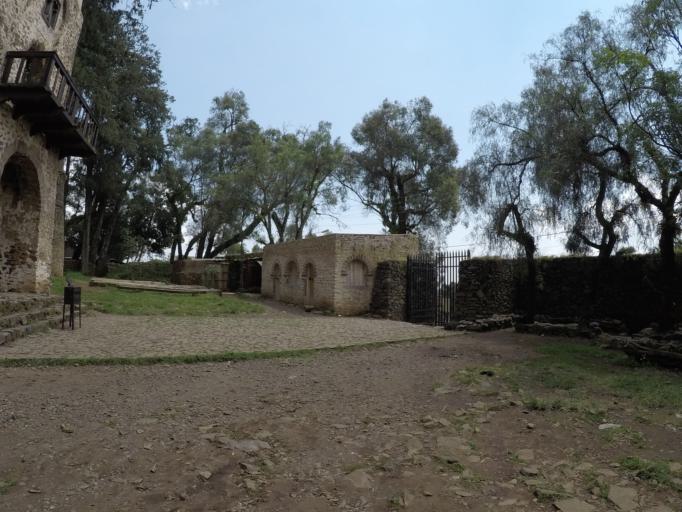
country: ET
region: Amhara
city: Gondar
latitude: 12.6126
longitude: 37.4801
